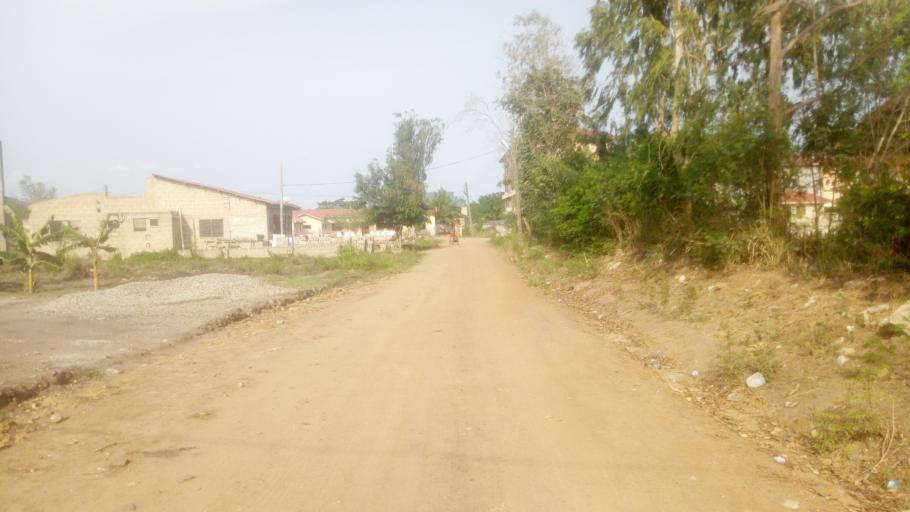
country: GH
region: Central
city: Winneba
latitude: 5.3786
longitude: -0.6392
